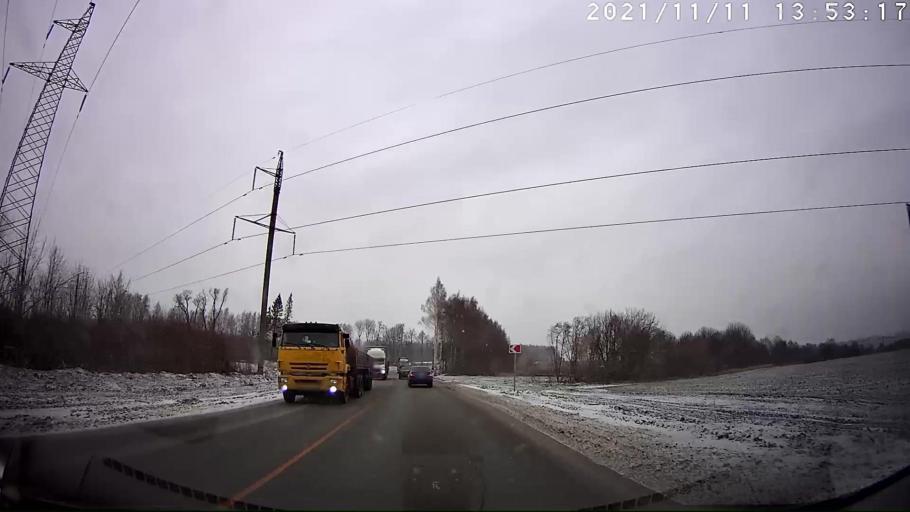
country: RU
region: Chuvashia
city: Shikhazany
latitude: 55.5759
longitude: 47.4137
